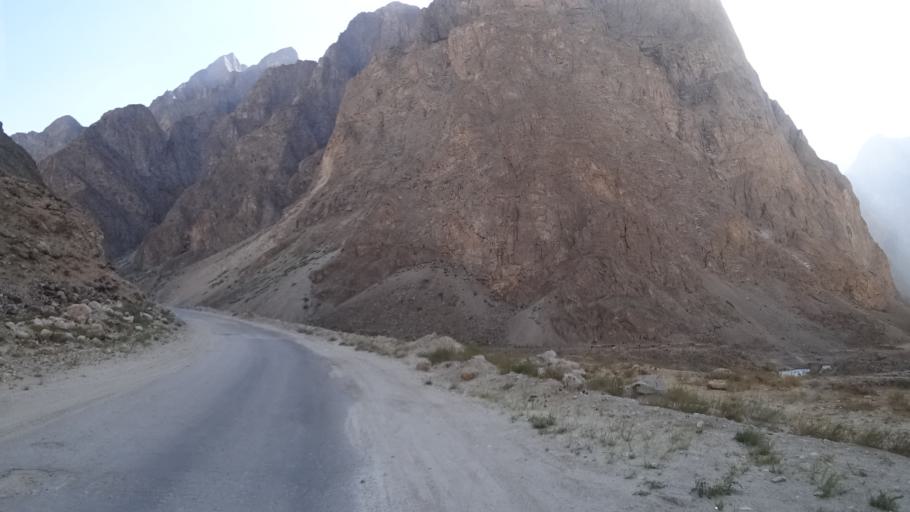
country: TJ
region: Gorno-Badakhshan
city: Rushon
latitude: 37.9921
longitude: 71.2706
